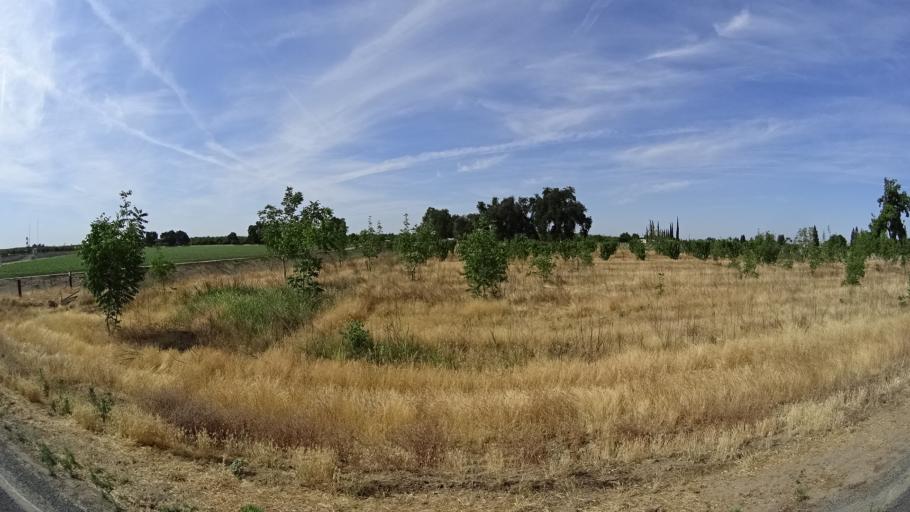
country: US
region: California
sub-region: Fresno County
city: Laton
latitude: 36.4157
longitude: -119.6699
